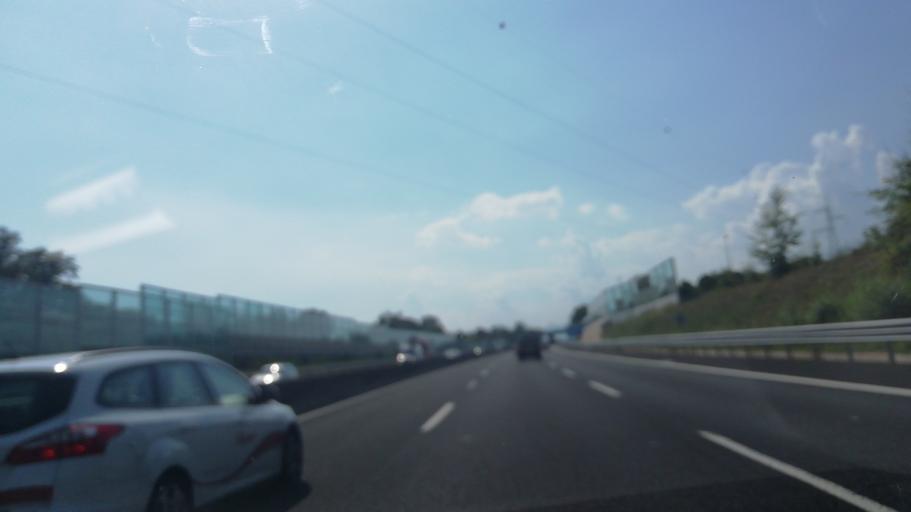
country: IT
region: Latium
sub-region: Provincia di Frosinone
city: Ceprano
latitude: 41.5428
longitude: 13.5005
